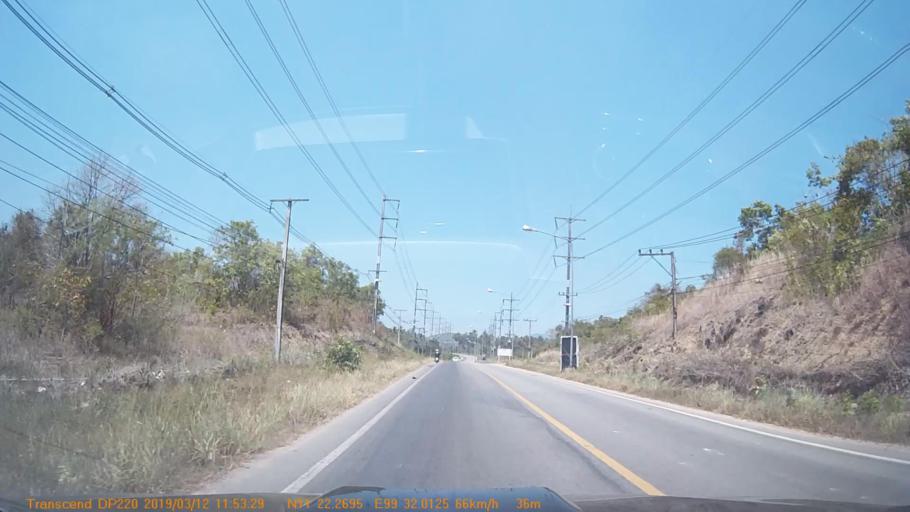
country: TH
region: Prachuap Khiri Khan
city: Thap Sakae
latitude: 11.3712
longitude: 99.5335
